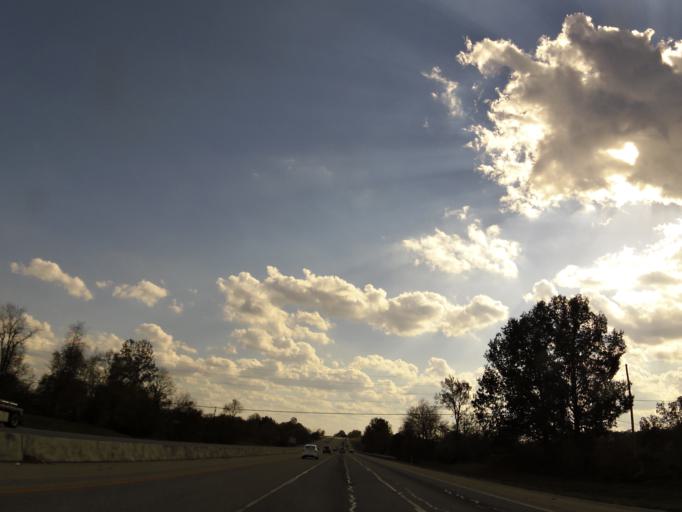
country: US
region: Kentucky
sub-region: Laurel County
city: London
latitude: 37.0790
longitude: -84.0994
